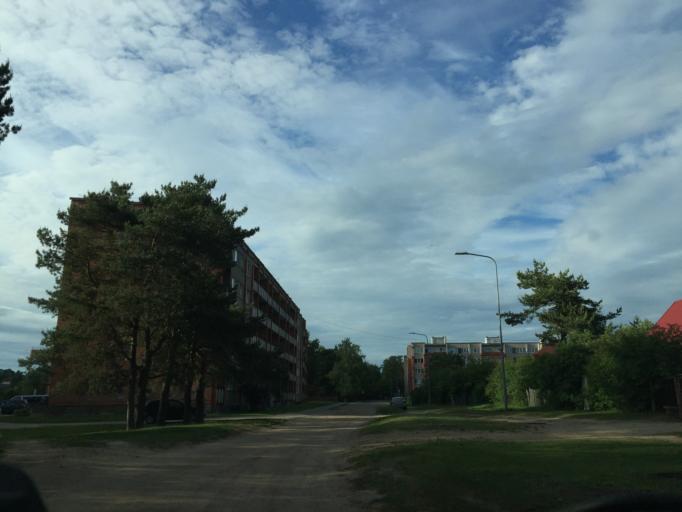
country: LV
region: Valmieras Rajons
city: Valmiera
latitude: 57.5289
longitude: 25.4184
